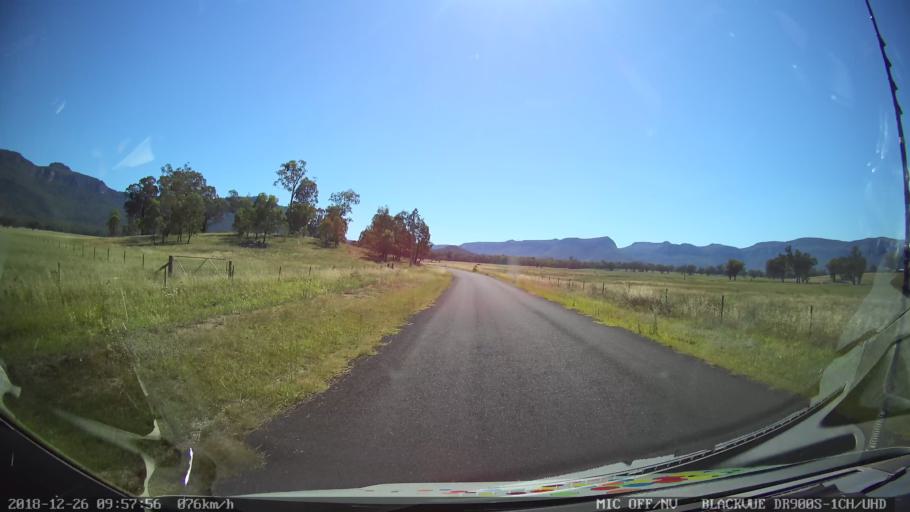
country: AU
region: New South Wales
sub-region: Mid-Western Regional
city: Kandos
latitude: -33.0403
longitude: 150.1988
